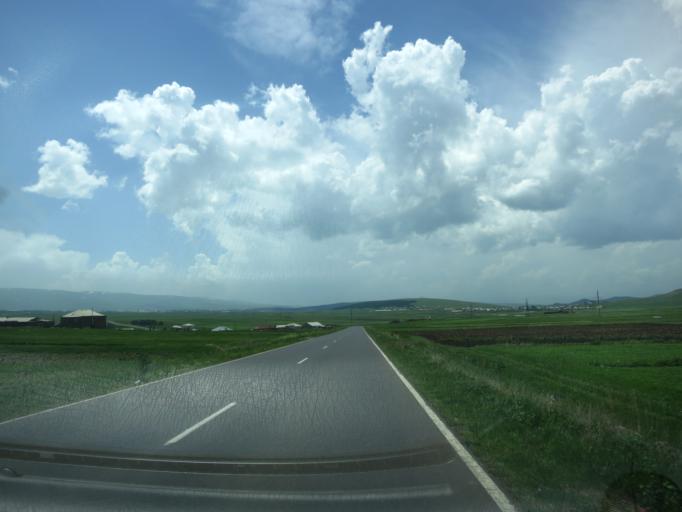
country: GE
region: Samtskhe-Javakheti
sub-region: Ninotsminda
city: Ninotsminda
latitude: 41.2953
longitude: 43.6518
